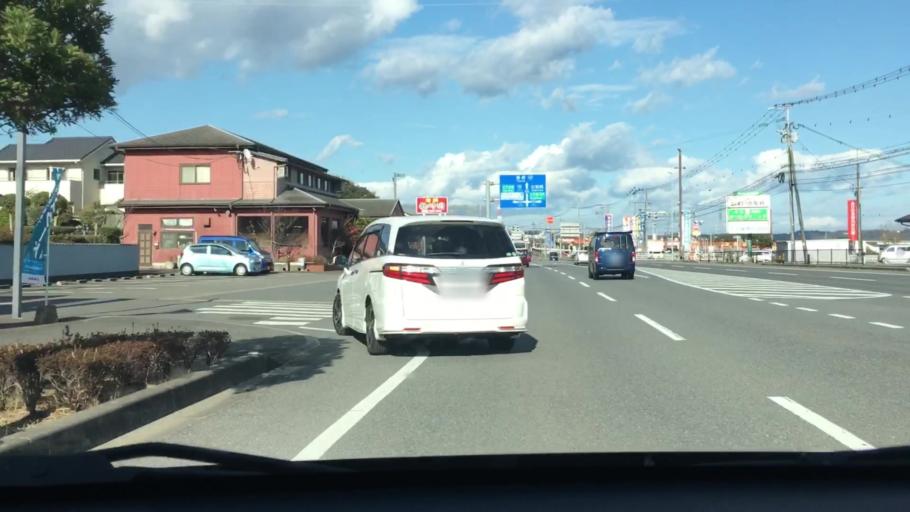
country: JP
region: Oita
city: Tsurusaki
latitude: 33.1892
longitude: 131.6710
